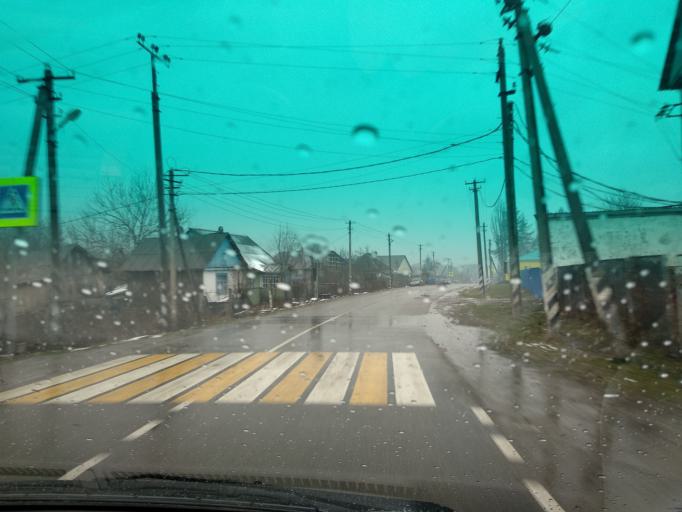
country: RU
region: Krasnodarskiy
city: Khadyzhensk
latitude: 44.2475
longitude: 39.3747
